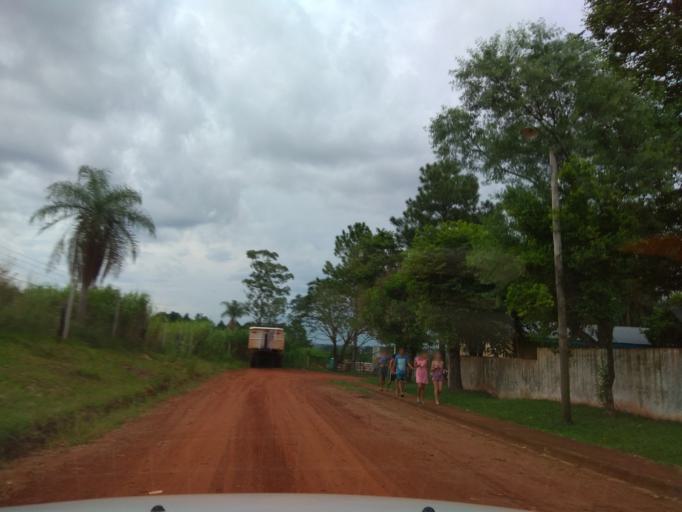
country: AR
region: Misiones
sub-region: Departamento de Capital
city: Posadas
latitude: -27.4384
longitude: -55.8923
